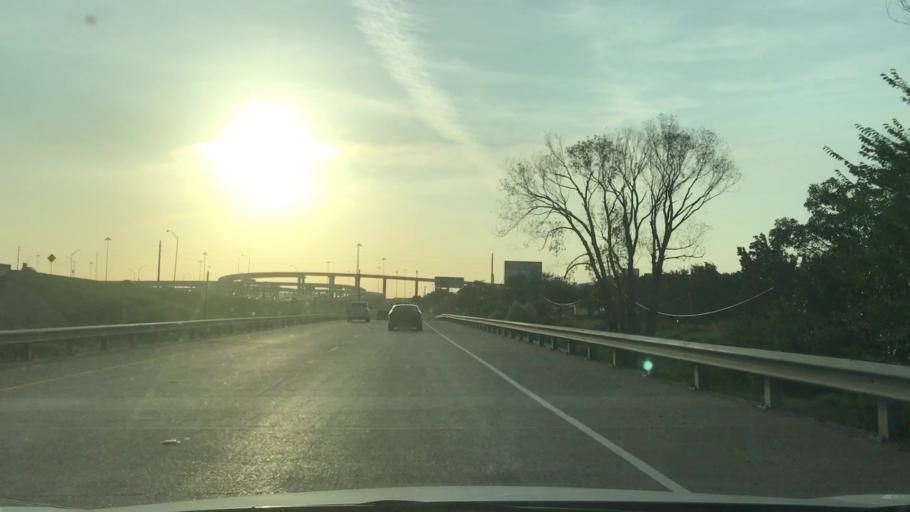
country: US
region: Texas
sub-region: Dallas County
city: Farmers Branch
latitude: 32.9066
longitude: -96.9087
